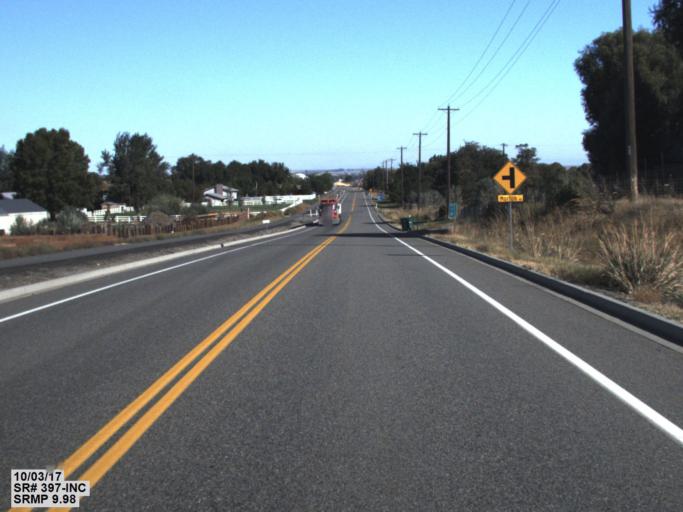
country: US
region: Washington
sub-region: Benton County
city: Finley
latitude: 46.1390
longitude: -119.0257
